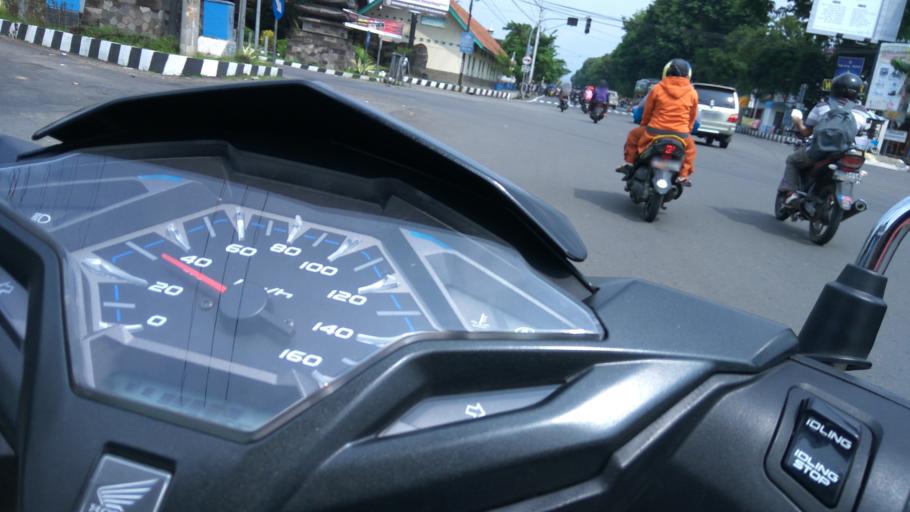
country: ID
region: Central Java
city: Jaten
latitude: -7.5895
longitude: 110.9267
